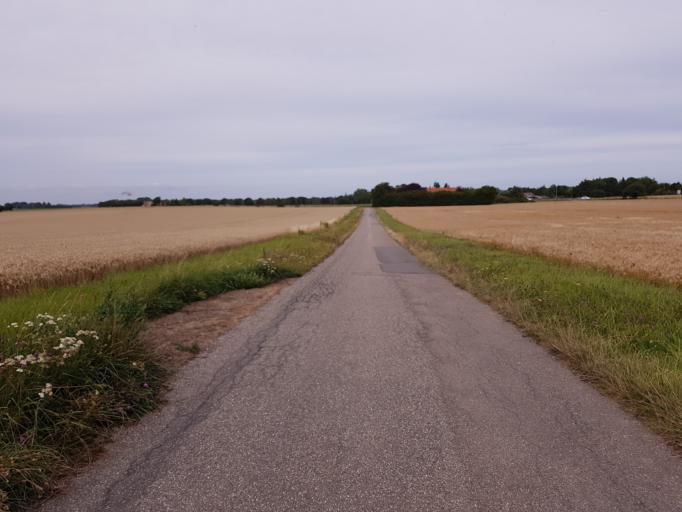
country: DK
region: Zealand
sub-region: Guldborgsund Kommune
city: Nykobing Falster
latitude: 54.5984
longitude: 11.9313
